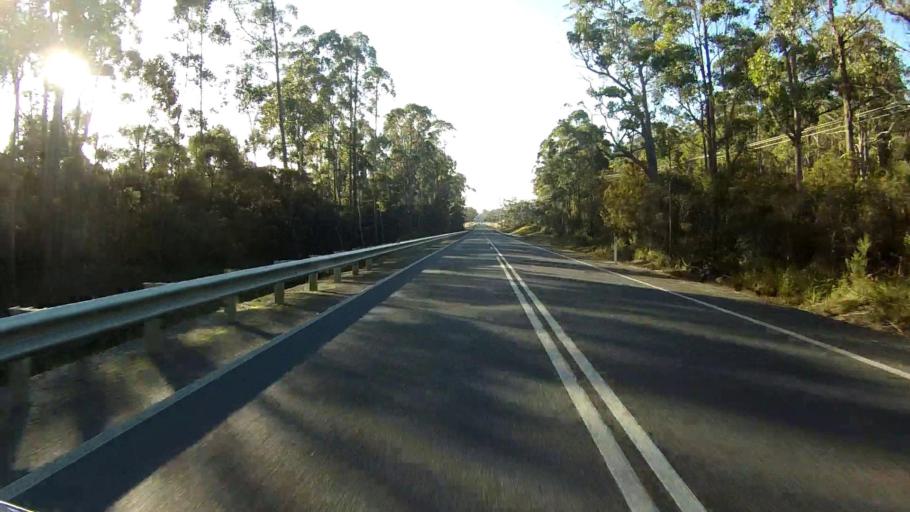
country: AU
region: Tasmania
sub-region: Clarence
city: Sandford
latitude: -43.0758
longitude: 147.8626
